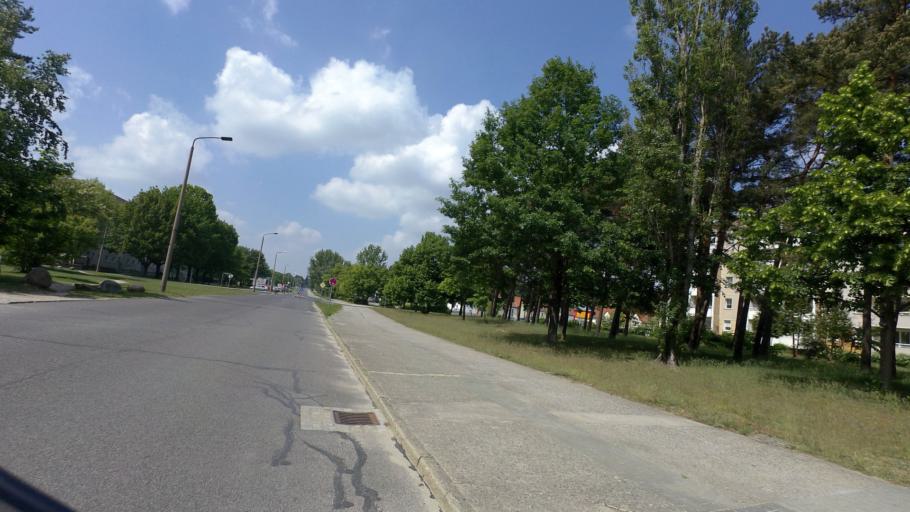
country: DE
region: Saxony
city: Weisswasser
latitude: 51.4934
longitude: 14.6397
